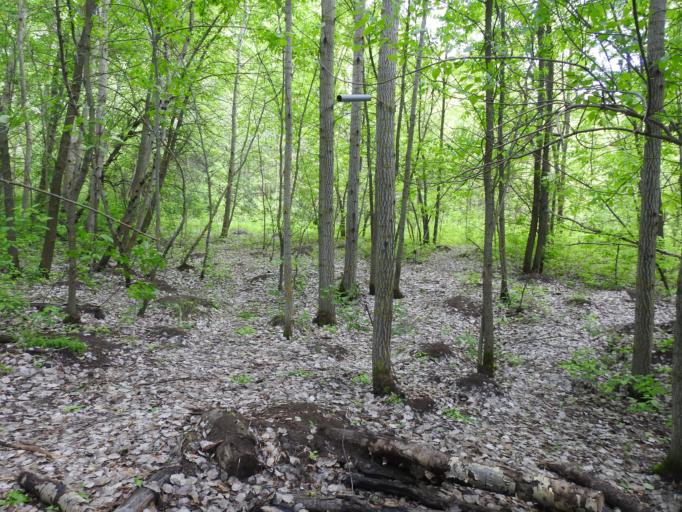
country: RU
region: Saratov
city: Engel's
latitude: 51.4693
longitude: 46.0726
